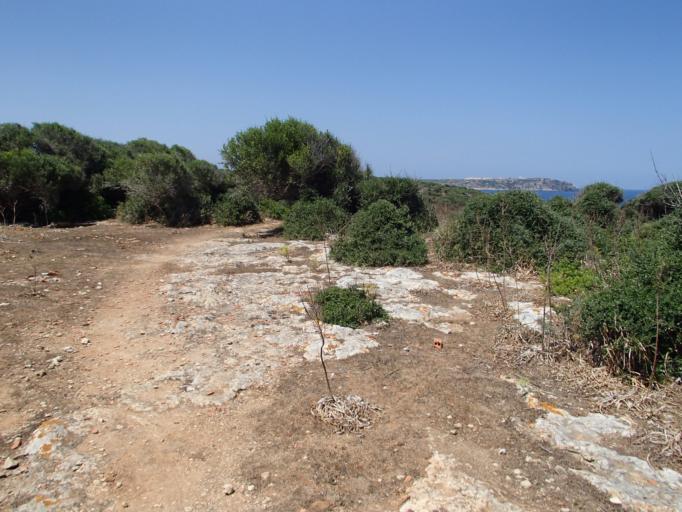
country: ES
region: Balearic Islands
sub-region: Illes Balears
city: Es Castell
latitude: 39.8460
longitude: 4.3029
